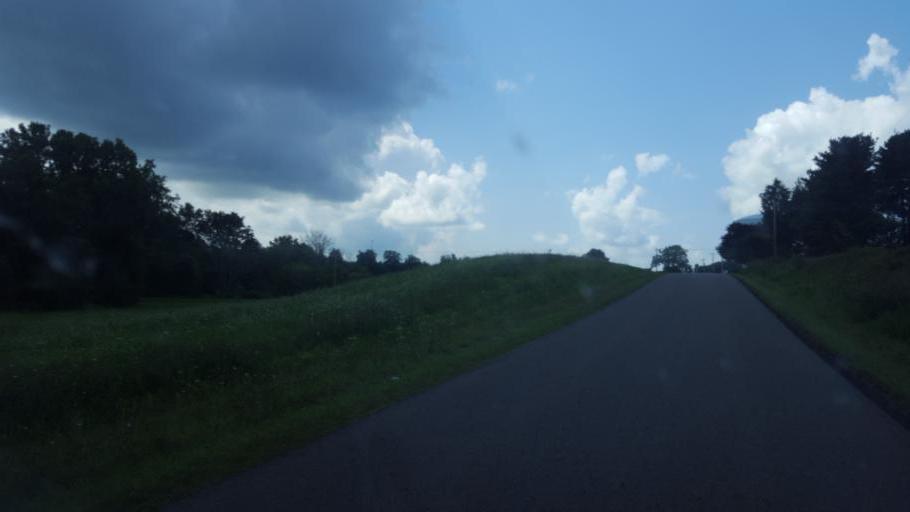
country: US
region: Ohio
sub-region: Knox County
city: Centerburg
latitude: 40.4087
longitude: -82.6780
